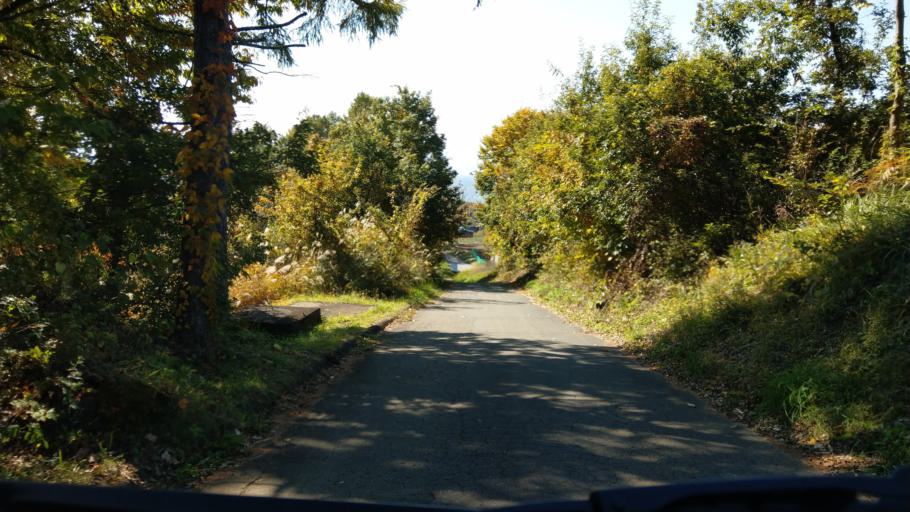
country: JP
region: Nagano
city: Komoro
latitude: 36.3559
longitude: 138.4434
